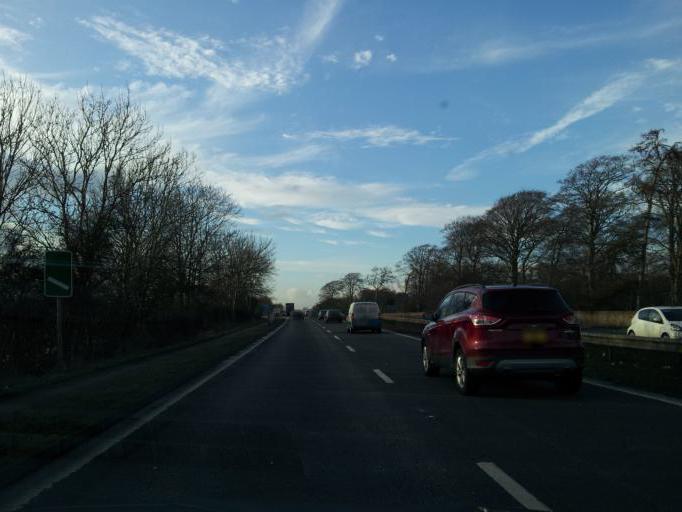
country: GB
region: England
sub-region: Peterborough
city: Wittering
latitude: 52.6256
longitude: -0.4636
